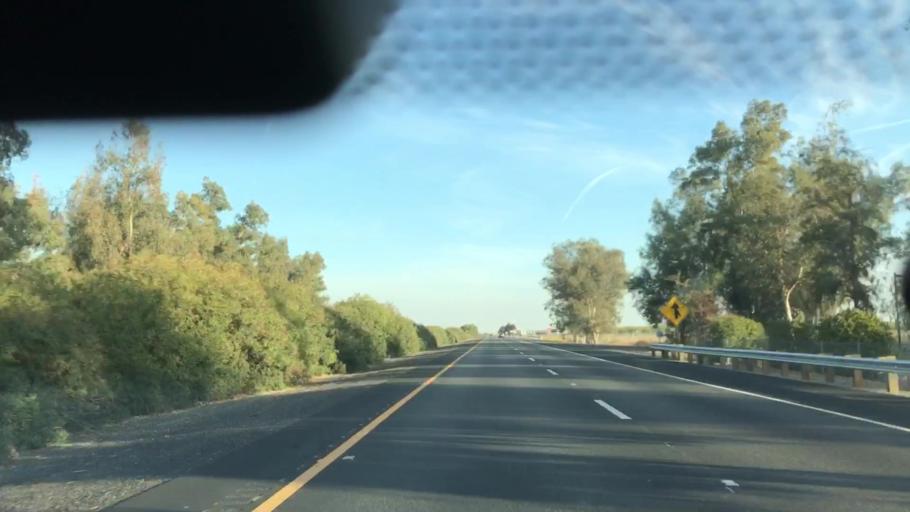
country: US
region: California
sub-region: Glenn County
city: Willows
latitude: 39.5928
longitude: -122.2092
